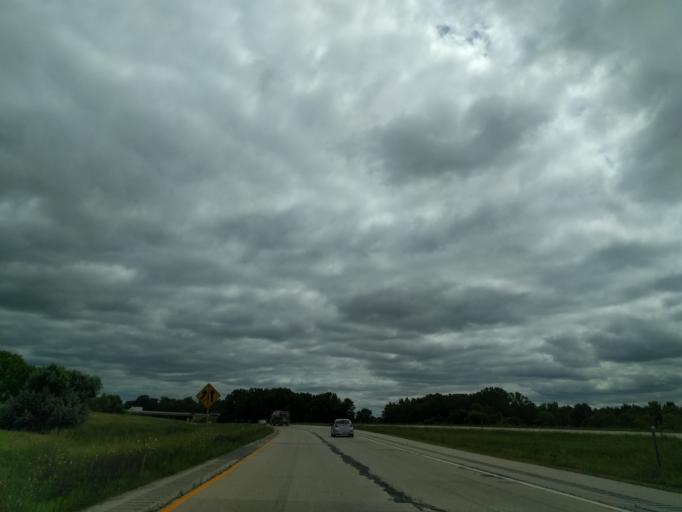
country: US
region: Wisconsin
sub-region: Brown County
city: Ashwaubenon
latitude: 44.4859
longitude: -88.0853
